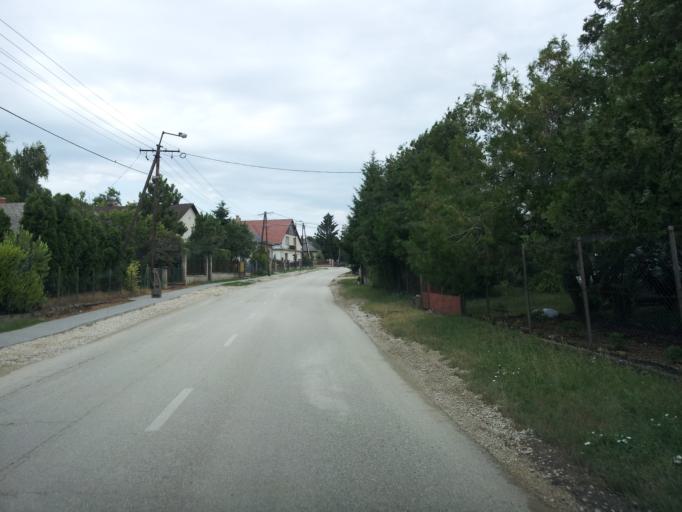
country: HU
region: Fejer
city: Lepseny
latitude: 47.0200
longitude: 18.2109
